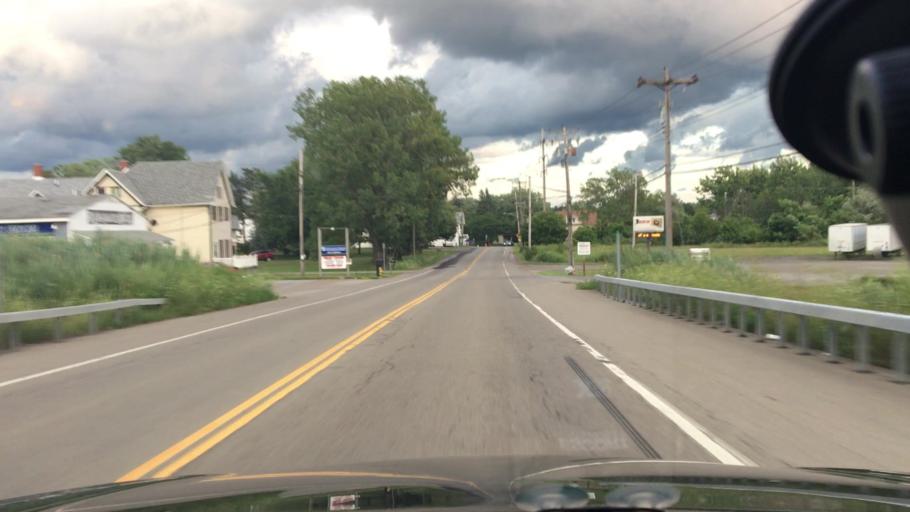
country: US
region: New York
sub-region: Erie County
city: West Seneca
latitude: 42.8379
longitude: -78.7782
